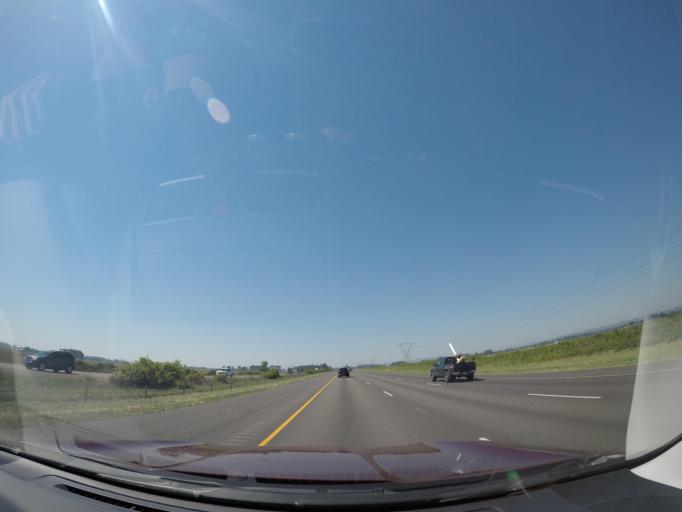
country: US
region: Oregon
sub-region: Marion County
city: Gervais
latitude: 45.0856
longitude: -122.9474
